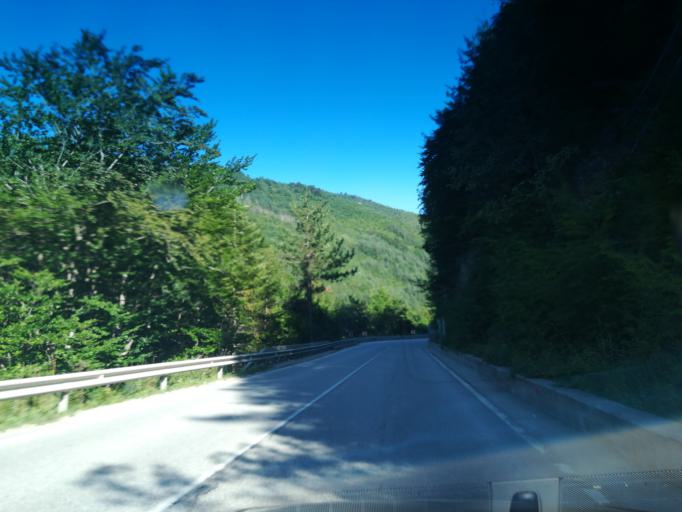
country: BG
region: Smolyan
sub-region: Obshtina Chepelare
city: Chepelare
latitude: 41.8180
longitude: 24.6991
